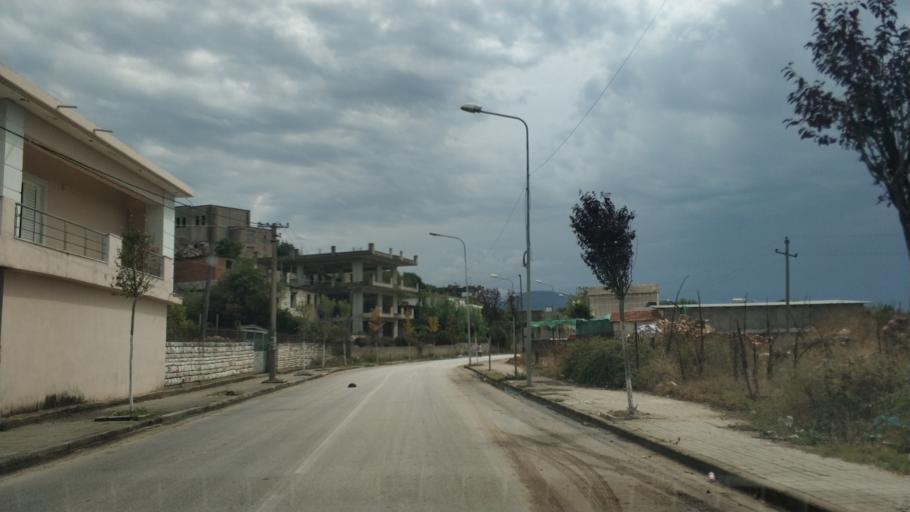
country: AL
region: Vlore
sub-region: Rrethi i Sarandes
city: Sarande
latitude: 39.8453
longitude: 20.0335
